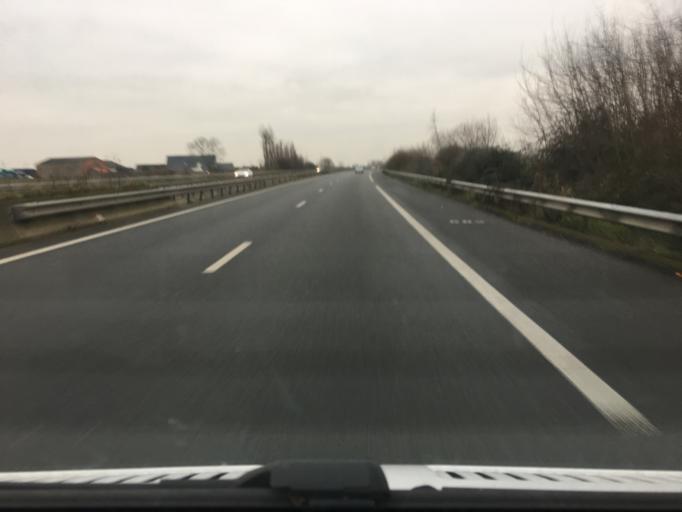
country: FR
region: Nord-Pas-de-Calais
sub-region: Departement du Nord
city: Quaedypre
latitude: 50.9355
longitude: 2.4656
